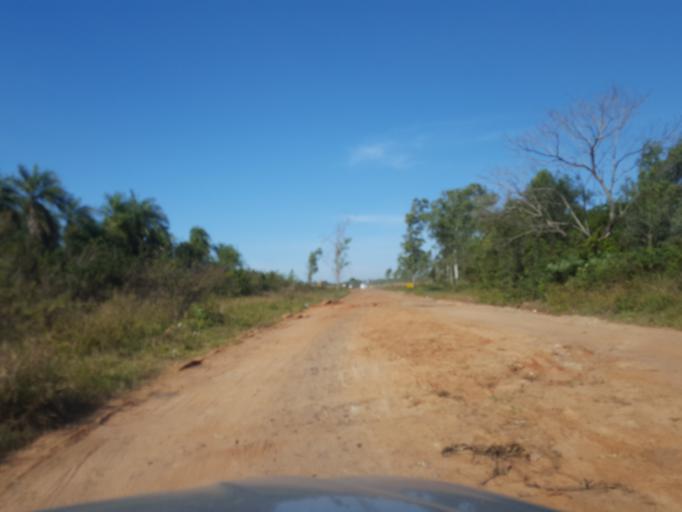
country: PY
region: Cordillera
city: Tobati
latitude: -25.2507
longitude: -57.1161
